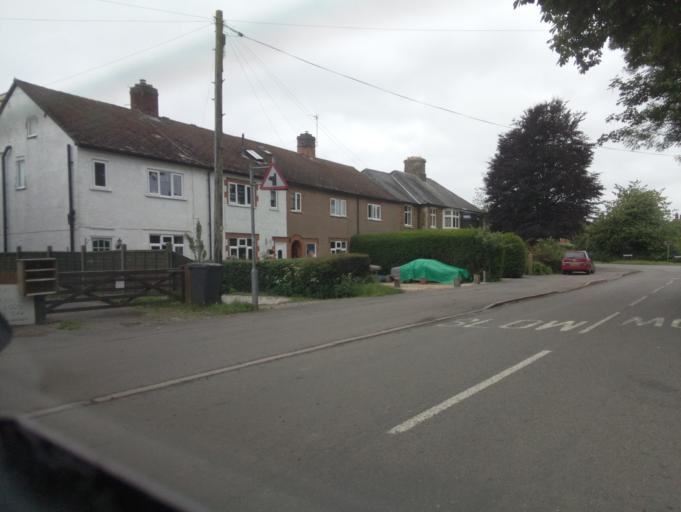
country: GB
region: England
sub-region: Leicestershire
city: Melton Mowbray
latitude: 52.6859
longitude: -0.8447
